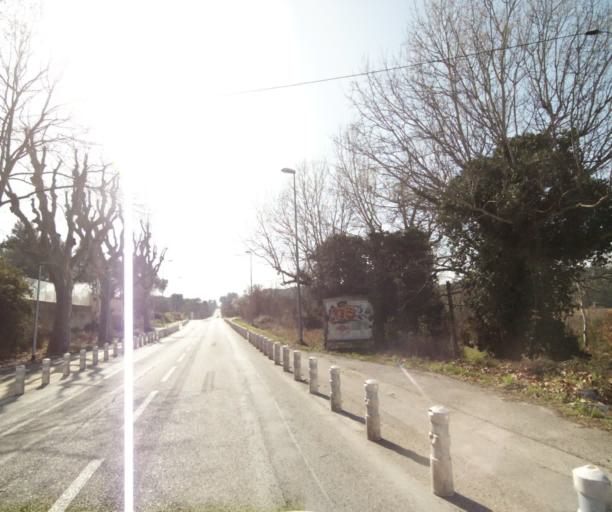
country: FR
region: Provence-Alpes-Cote d'Azur
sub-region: Departement des Bouches-du-Rhone
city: Aix-en-Provence
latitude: 43.5054
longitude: 5.4355
